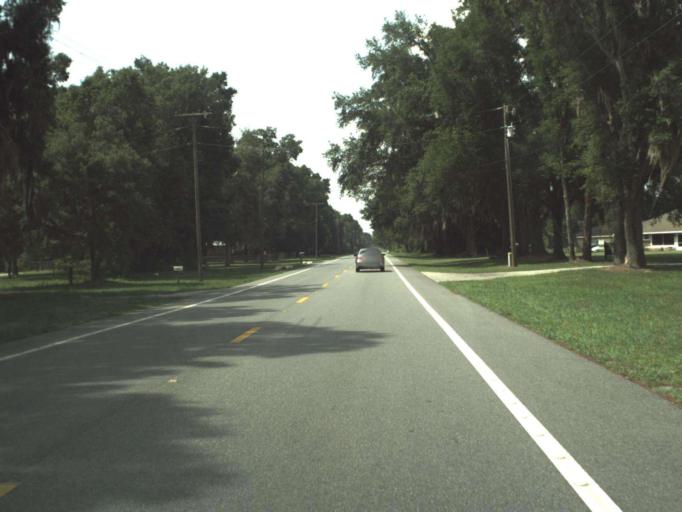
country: US
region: Florida
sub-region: Sumter County
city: Bushnell
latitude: 28.7010
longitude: -82.1043
